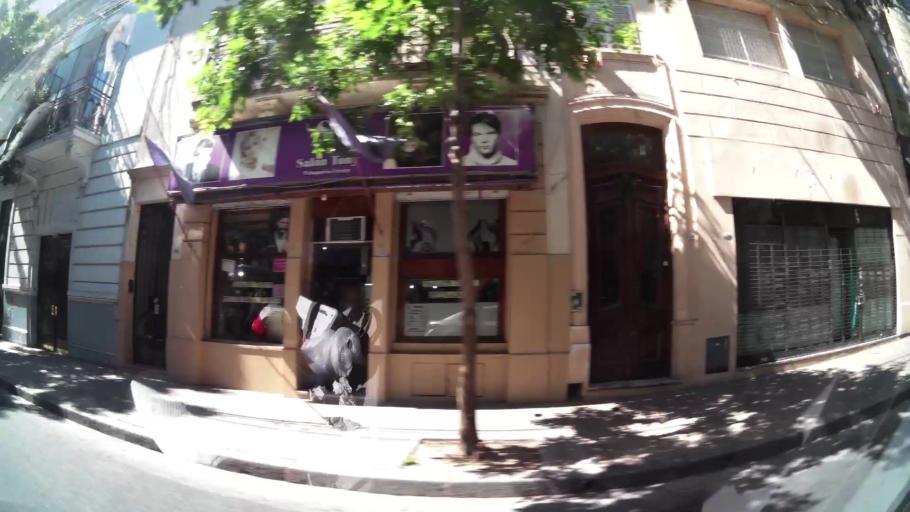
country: AR
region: Buenos Aires F.D.
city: Buenos Aires
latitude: -34.6210
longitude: -58.3835
